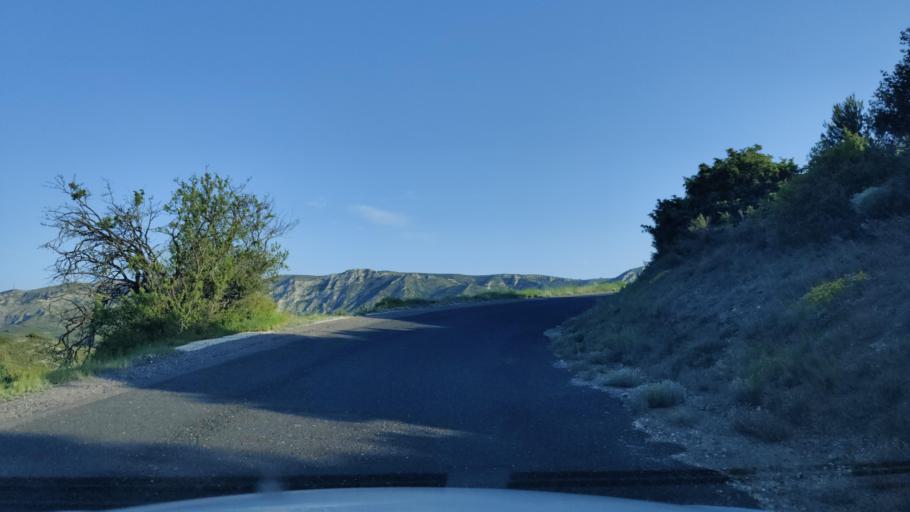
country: FR
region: Languedoc-Roussillon
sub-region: Departement des Pyrenees-Orientales
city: Estagel
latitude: 42.7863
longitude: 2.7519
